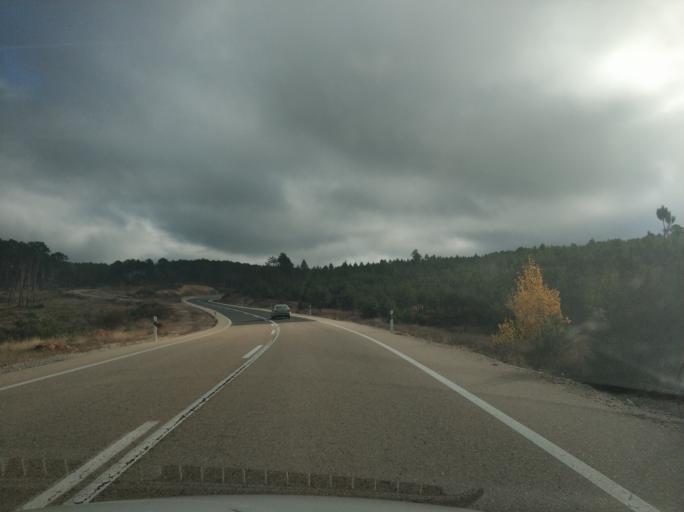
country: ES
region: Castille and Leon
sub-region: Provincia de Soria
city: Navaleno
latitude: 41.8279
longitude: -2.9576
